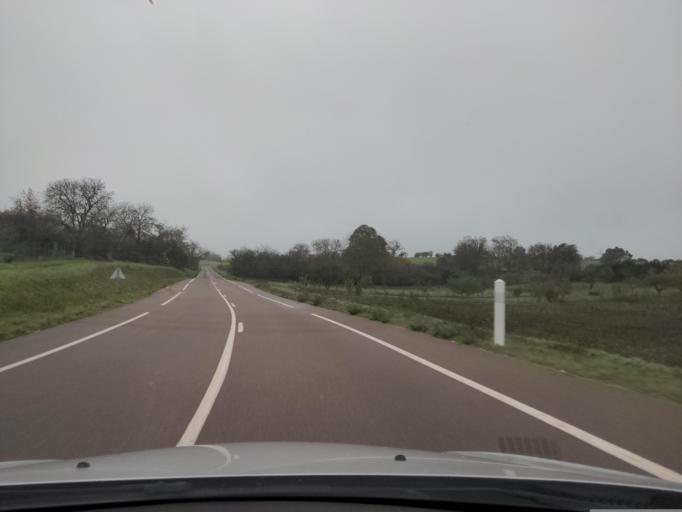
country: FR
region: Bourgogne
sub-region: Departement de la Cote-d'Or
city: Ruffey-les-Echirey
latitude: 47.3695
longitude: 5.0734
